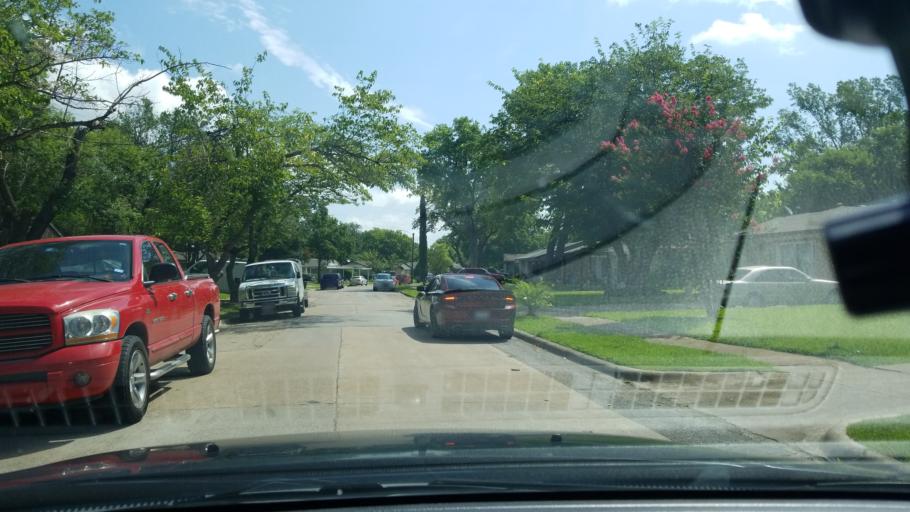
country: US
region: Texas
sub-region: Dallas County
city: Mesquite
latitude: 32.8132
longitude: -96.6560
